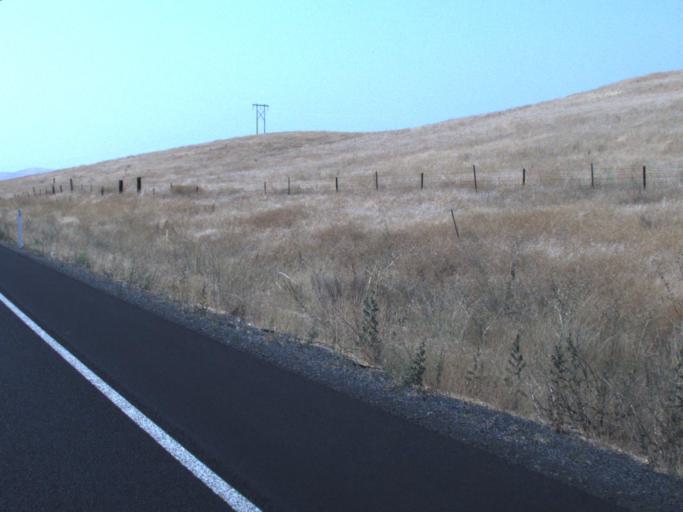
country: US
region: Washington
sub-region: Yakima County
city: Granger
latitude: 46.5032
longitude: -120.1177
